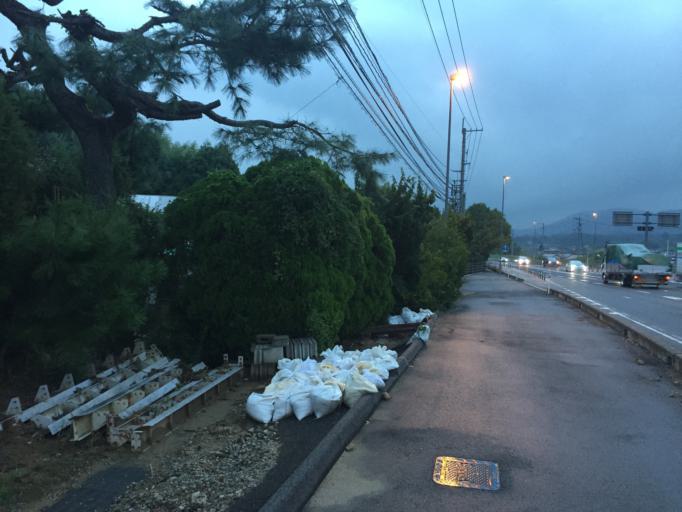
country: JP
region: Hiroshima
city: Takehara
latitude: 34.3979
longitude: 132.7650
